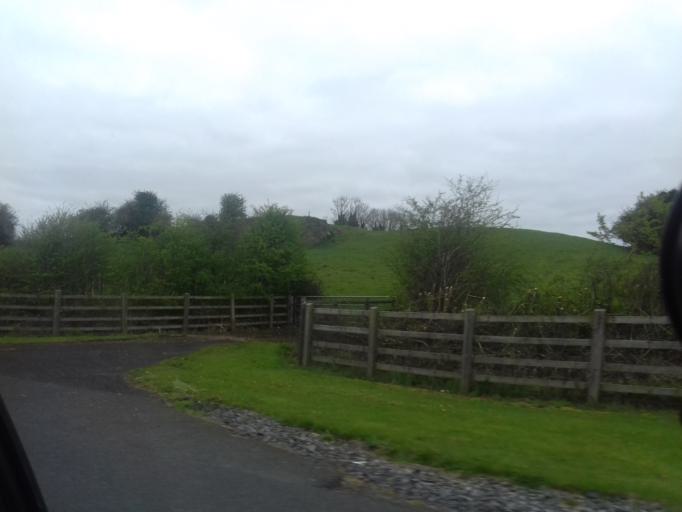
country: IE
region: Leinster
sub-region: An Iarmhi
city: An Muileann gCearr
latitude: 53.5153
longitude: -7.2728
